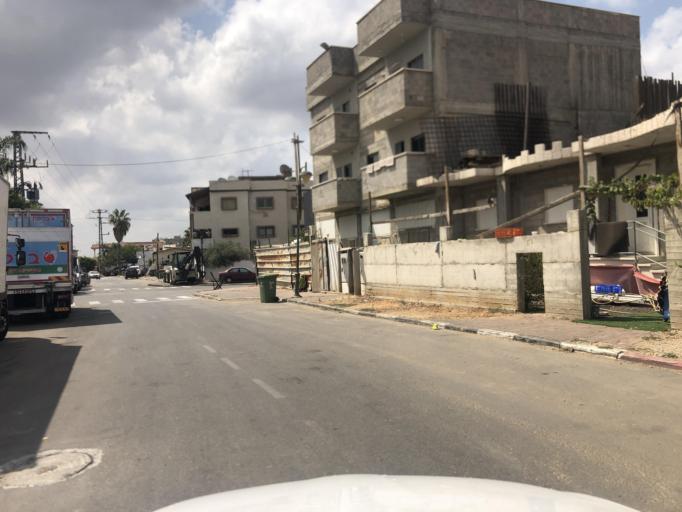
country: IL
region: Central District
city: Jaljulya
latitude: 32.1535
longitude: 34.9574
